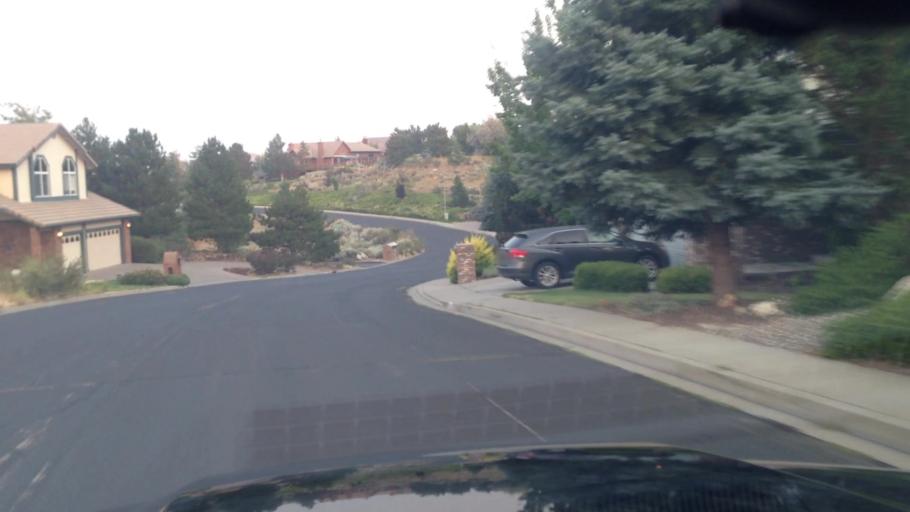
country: US
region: Nevada
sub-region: Washoe County
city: Reno
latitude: 39.4846
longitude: -119.8501
